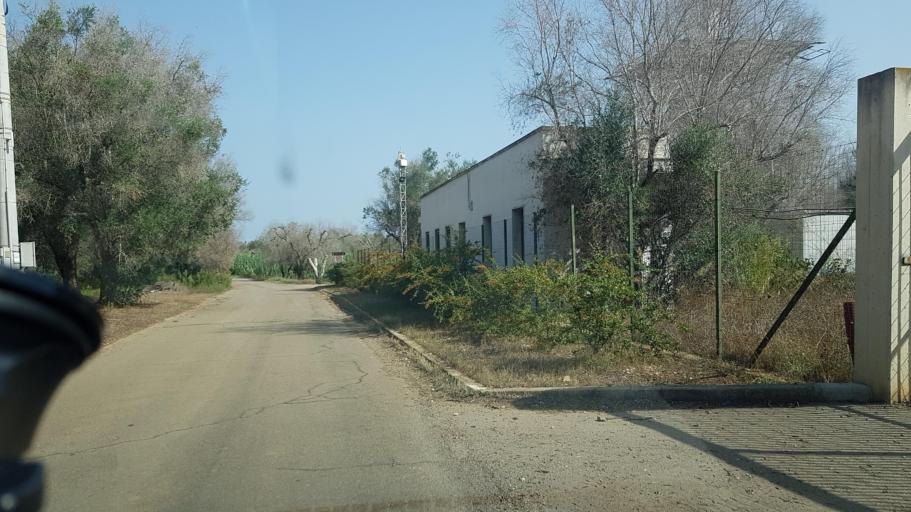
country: IT
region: Apulia
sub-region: Provincia di Brindisi
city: Torchiarolo
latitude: 40.5061
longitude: 18.0595
